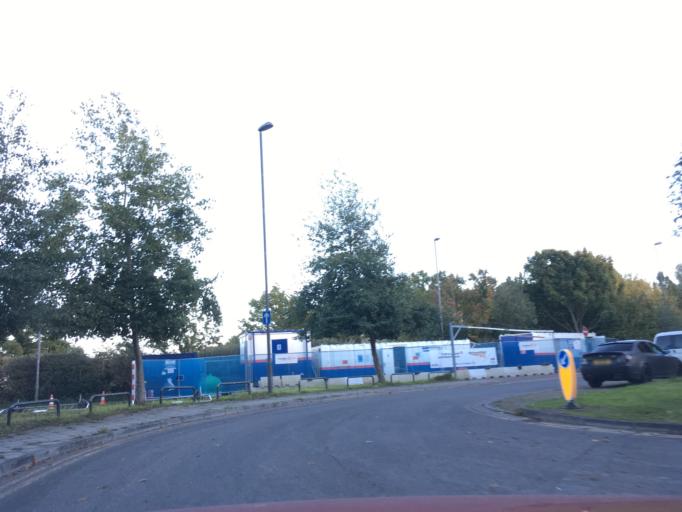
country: GB
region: England
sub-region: South Gloucestershire
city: Stoke Gifford
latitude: 51.5058
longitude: -2.5628
